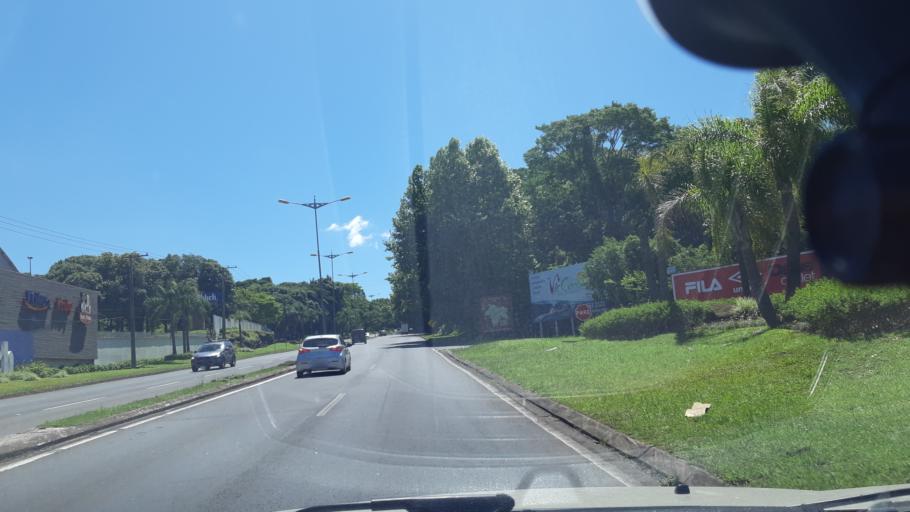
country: BR
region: Rio Grande do Sul
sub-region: Ivoti
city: Ivoti
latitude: -29.6262
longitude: -51.1374
